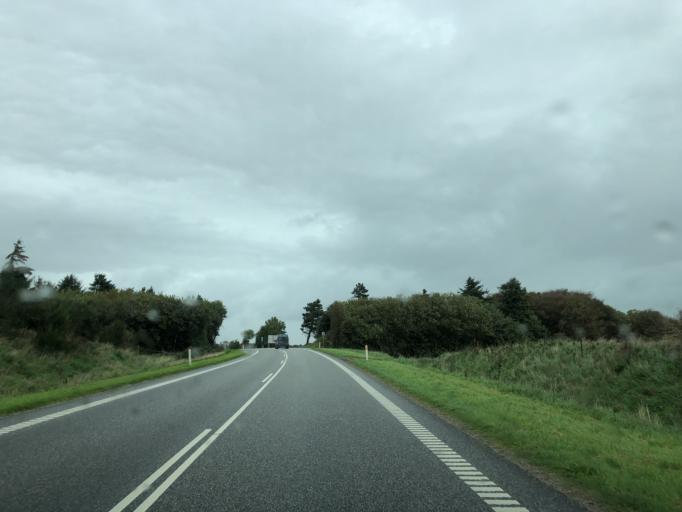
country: DK
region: Central Jutland
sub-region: Struer Kommune
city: Struer
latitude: 56.6035
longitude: 8.5288
